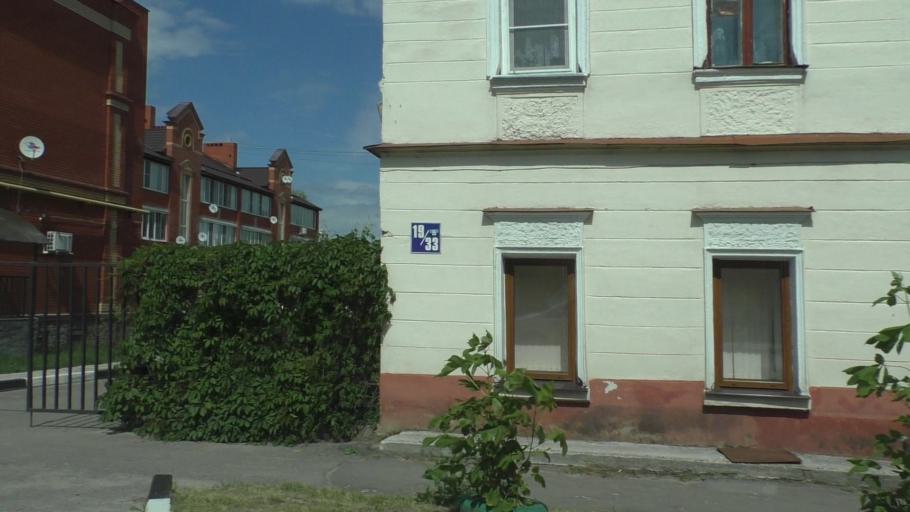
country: RU
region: Moskovskaya
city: Yegor'yevsk
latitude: 55.3852
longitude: 39.0361
